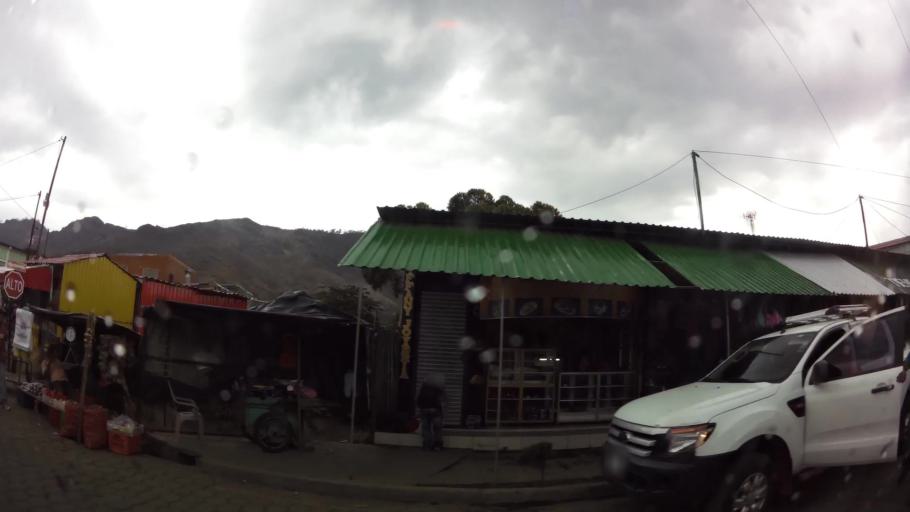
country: NI
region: Jinotega
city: Jinotega
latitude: 13.0931
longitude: -85.9992
